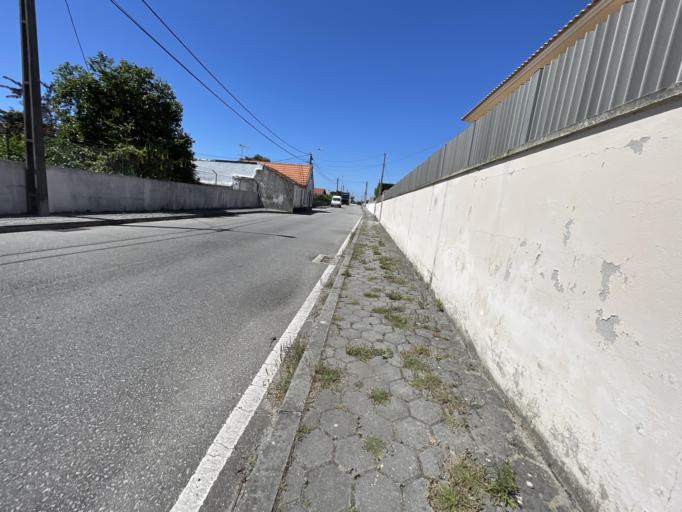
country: PT
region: Aveiro
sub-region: Ovar
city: Cortegaca
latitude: 40.9443
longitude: -8.6262
